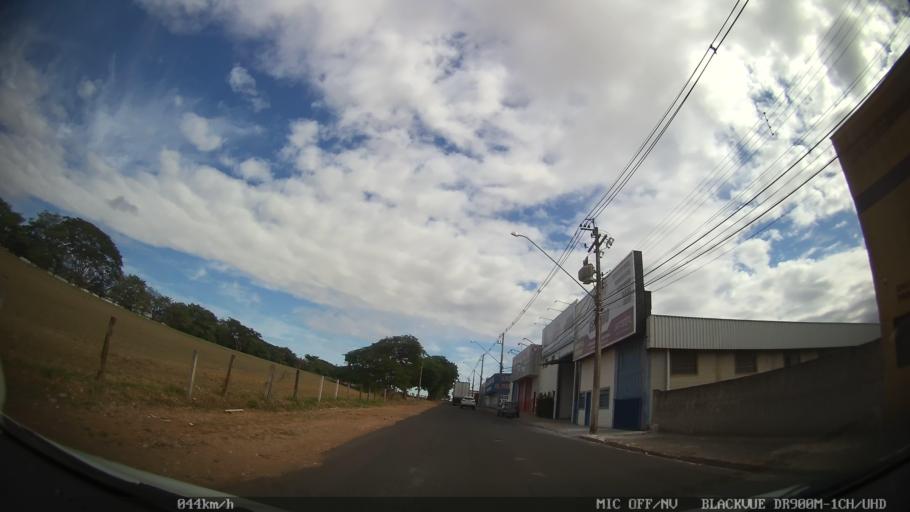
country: BR
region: Sao Paulo
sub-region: Sao Jose Do Rio Preto
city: Sao Jose do Rio Preto
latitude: -20.8086
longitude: -49.5010
